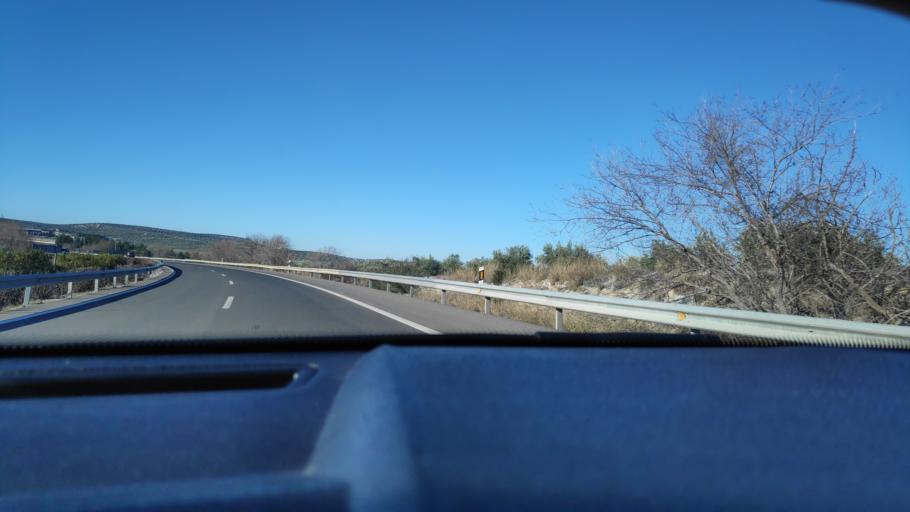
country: ES
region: Andalusia
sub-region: Provincia de Jaen
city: Torre del Campo
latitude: 37.7829
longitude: -3.8909
